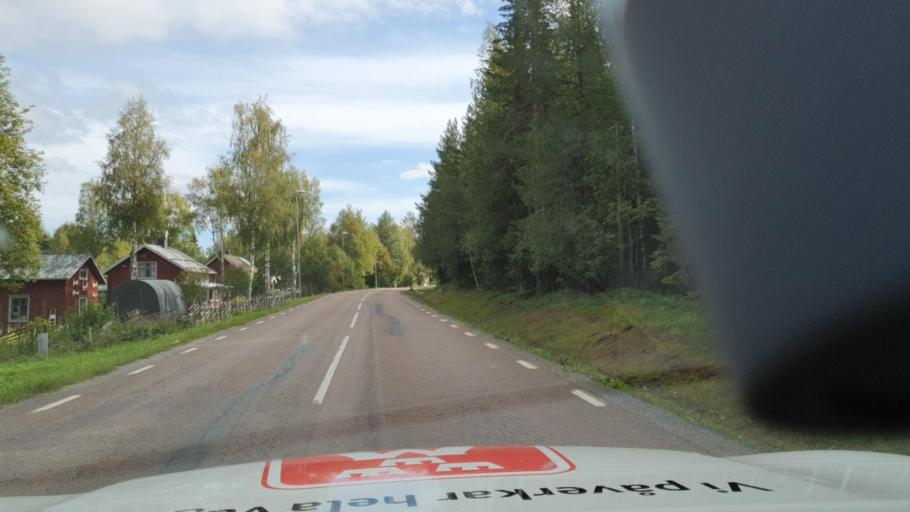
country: SE
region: Jaemtland
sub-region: Stroemsunds Kommun
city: Stroemsund
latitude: 63.8083
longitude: 15.6820
